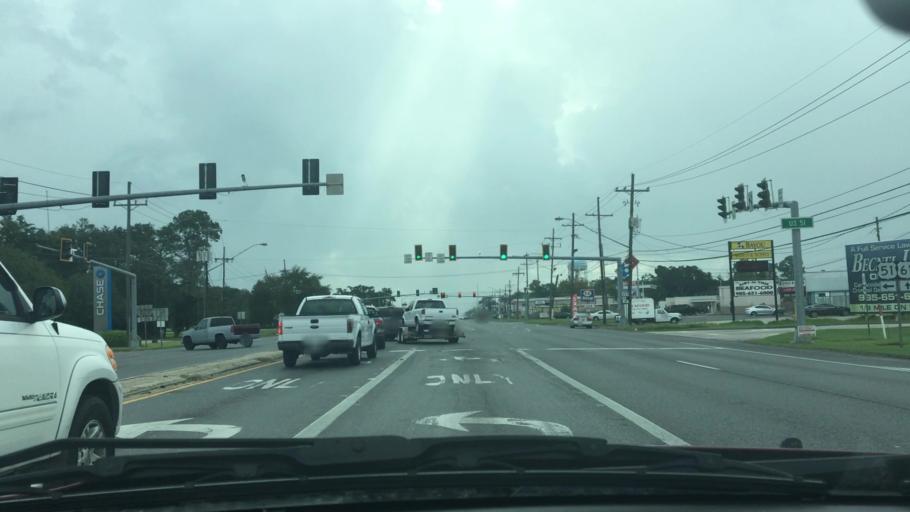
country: US
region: Louisiana
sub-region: Saint John the Baptist Parish
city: Laplace
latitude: 30.0674
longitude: -90.4818
